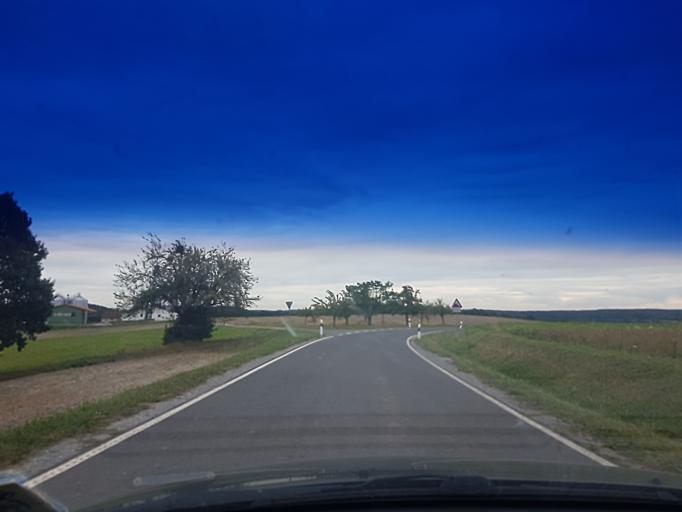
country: DE
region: Bavaria
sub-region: Regierungsbezirk Unterfranken
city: Geiselwind
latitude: 49.7968
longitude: 10.4891
